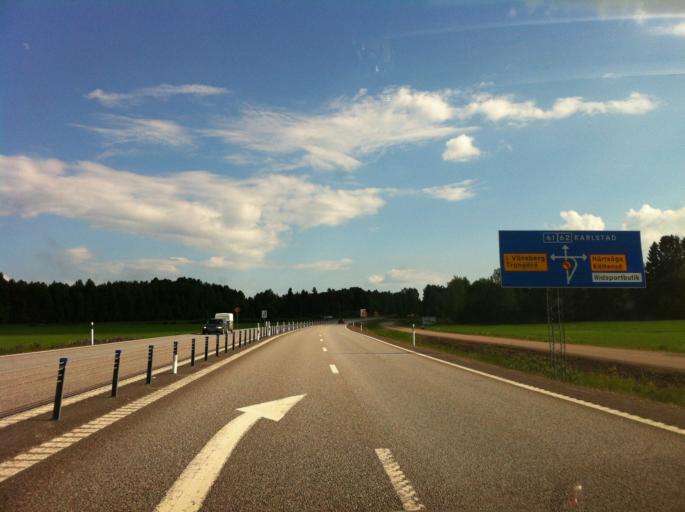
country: SE
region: Vaermland
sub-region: Karlstads Kommun
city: Karlstad
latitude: 59.4253
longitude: 13.4091
